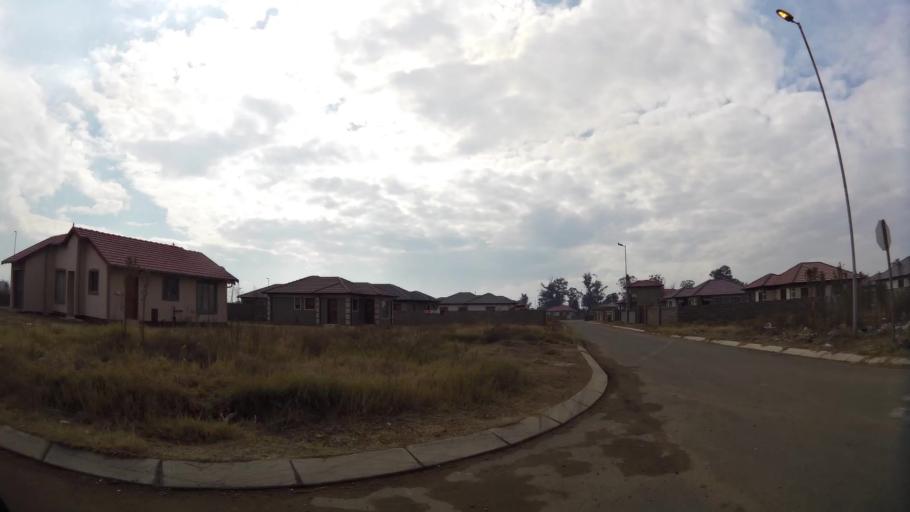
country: ZA
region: Gauteng
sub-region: Sedibeng District Municipality
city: Vanderbijlpark
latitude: -26.6811
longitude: 27.8433
